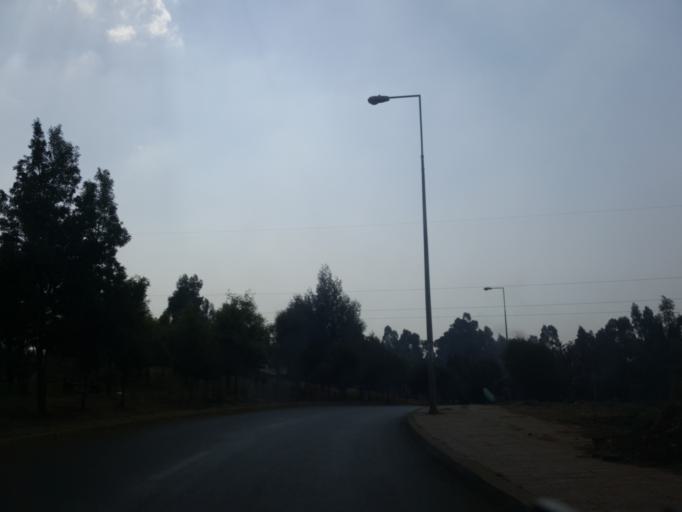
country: ET
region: Adis Abeba
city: Addis Ababa
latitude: 9.0691
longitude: 38.7208
